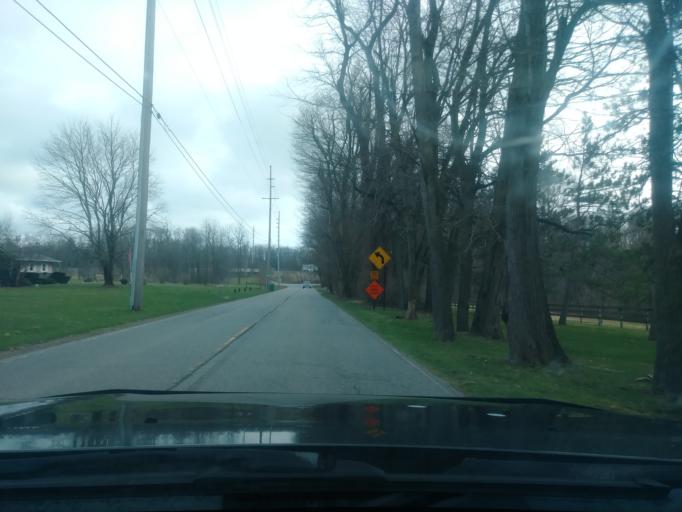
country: US
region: Indiana
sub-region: LaPorte County
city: LaPorte
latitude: 41.6316
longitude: -86.7967
